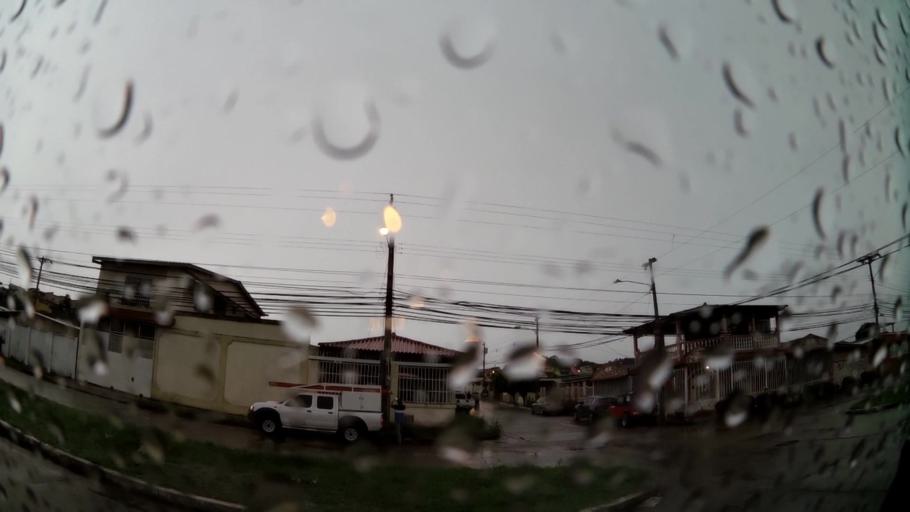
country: PA
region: Panama
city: San Miguelito
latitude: 9.0566
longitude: -79.4742
